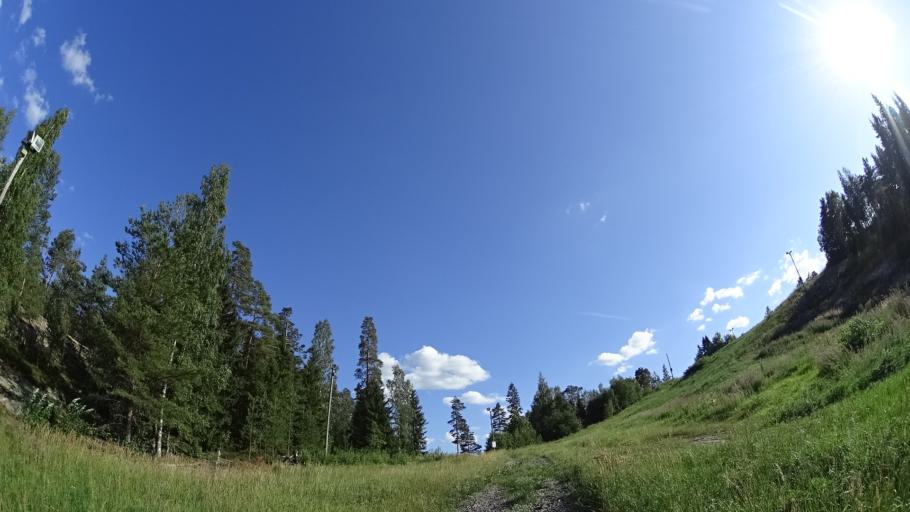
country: FI
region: Uusimaa
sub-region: Helsinki
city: Vihti
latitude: 60.3771
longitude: 24.3707
